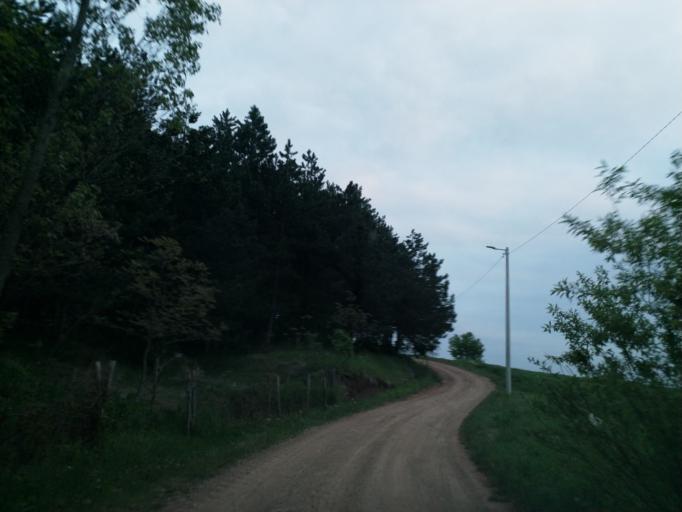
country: RS
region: Central Serbia
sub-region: Pomoravski Okrug
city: Paracin
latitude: 43.9417
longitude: 21.5119
